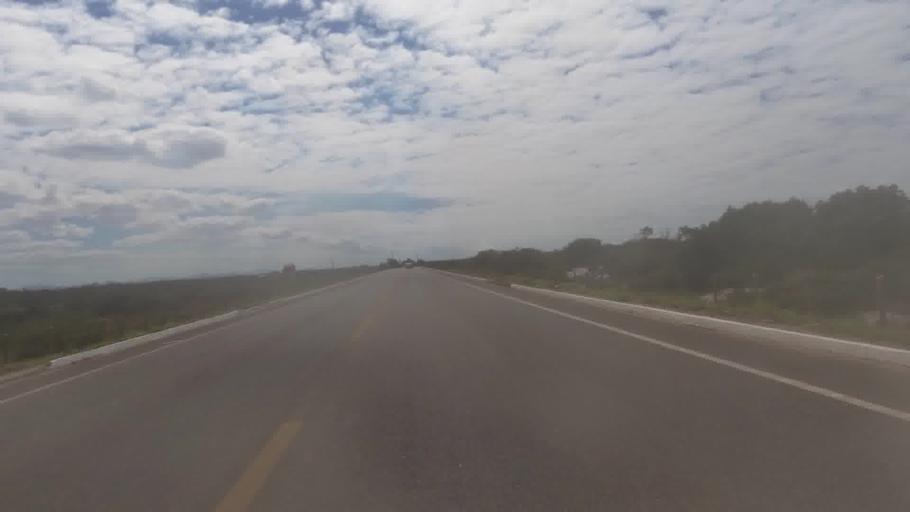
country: BR
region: Espirito Santo
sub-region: Marataizes
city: Marataizes
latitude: -21.2323
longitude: -40.9762
